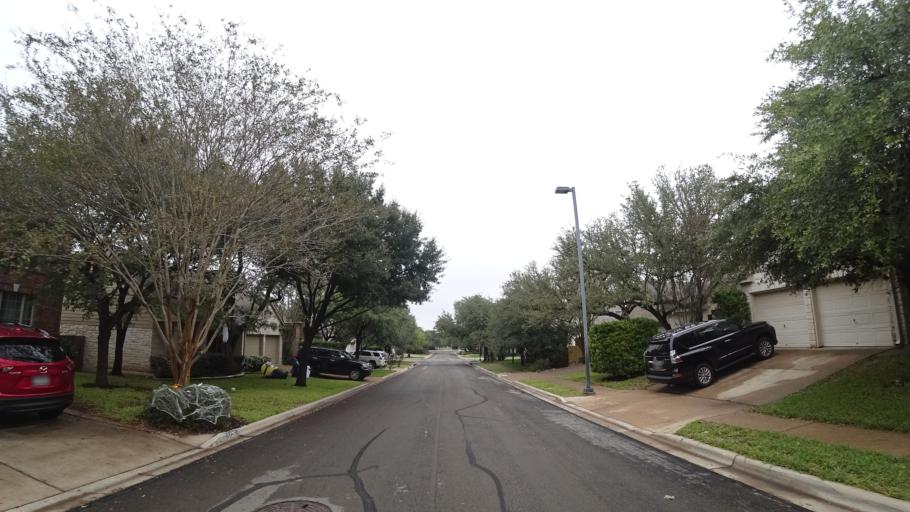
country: US
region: Texas
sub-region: Travis County
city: Shady Hollow
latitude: 30.1922
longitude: -97.8699
